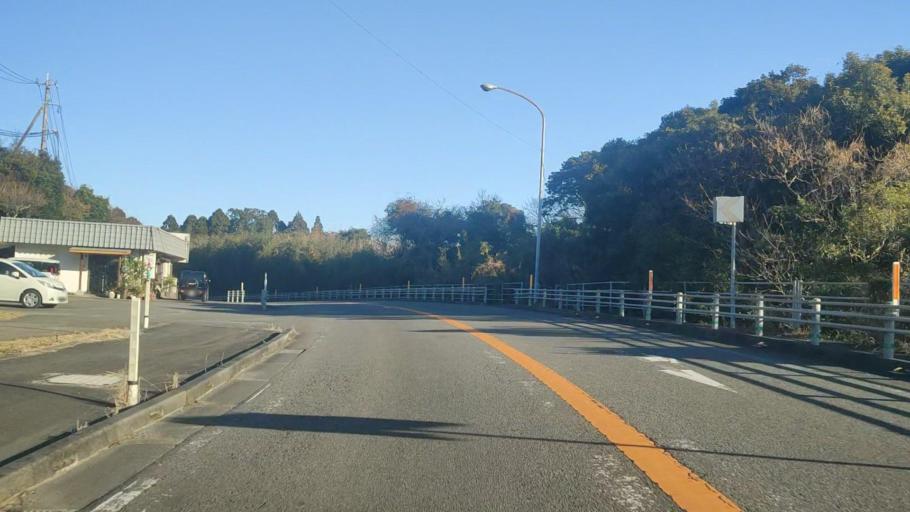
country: JP
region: Miyazaki
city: Nobeoka
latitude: 32.3442
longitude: 131.6244
